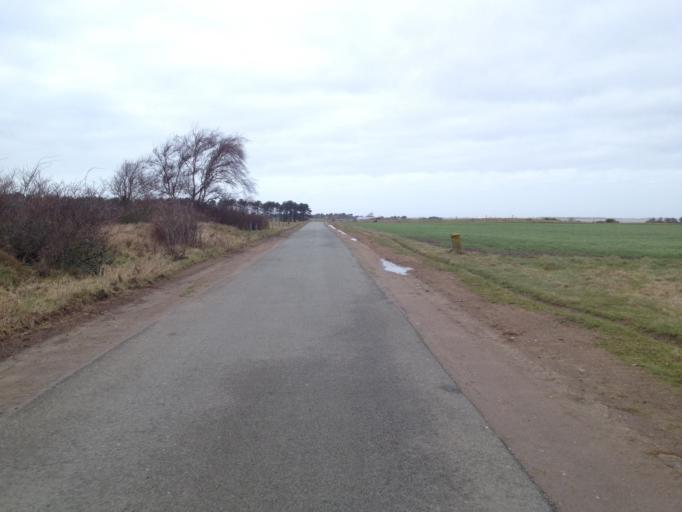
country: DE
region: Schleswig-Holstein
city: Nebel
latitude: 54.6653
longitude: 8.3453
